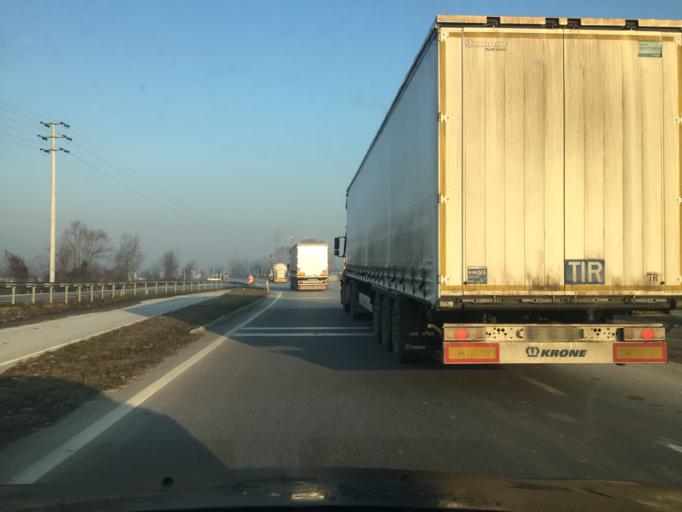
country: TR
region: Sakarya
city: Akyazi
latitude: 40.6728
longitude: 30.5869
